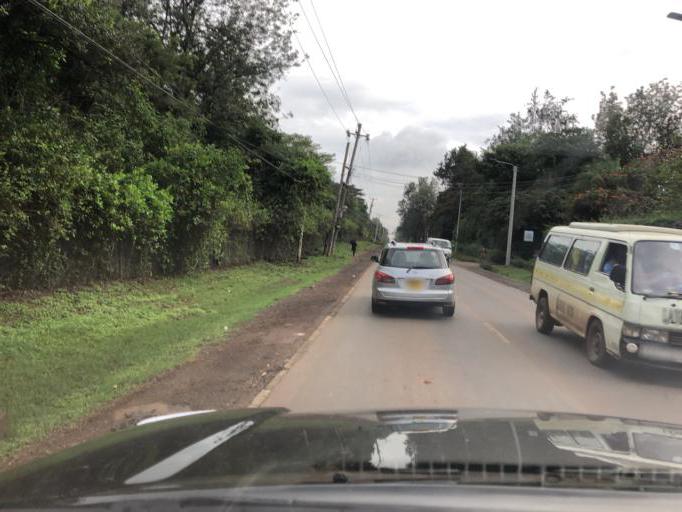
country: KE
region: Kajiado
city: Ngong
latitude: -1.3435
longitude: 36.7147
